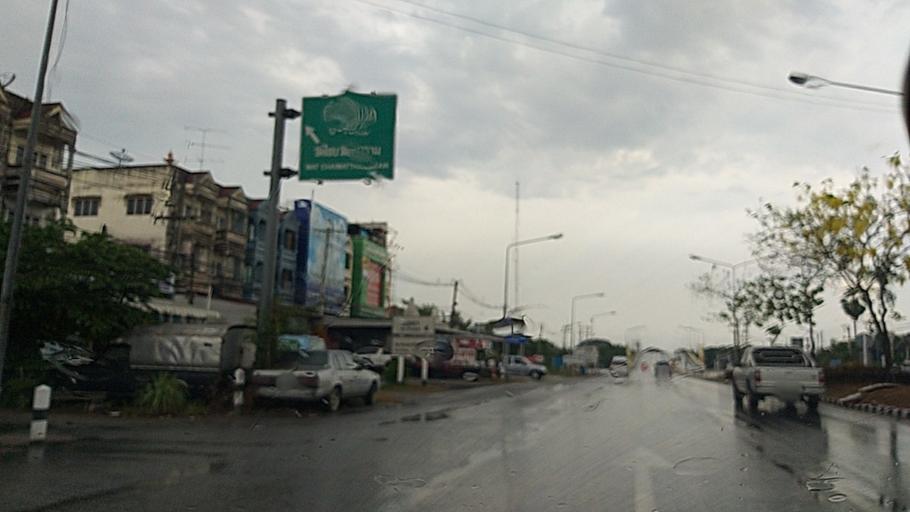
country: TH
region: Phra Nakhon Si Ayutthaya
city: Phra Nakhon Si Ayutthaya
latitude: 14.3505
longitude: 100.5421
